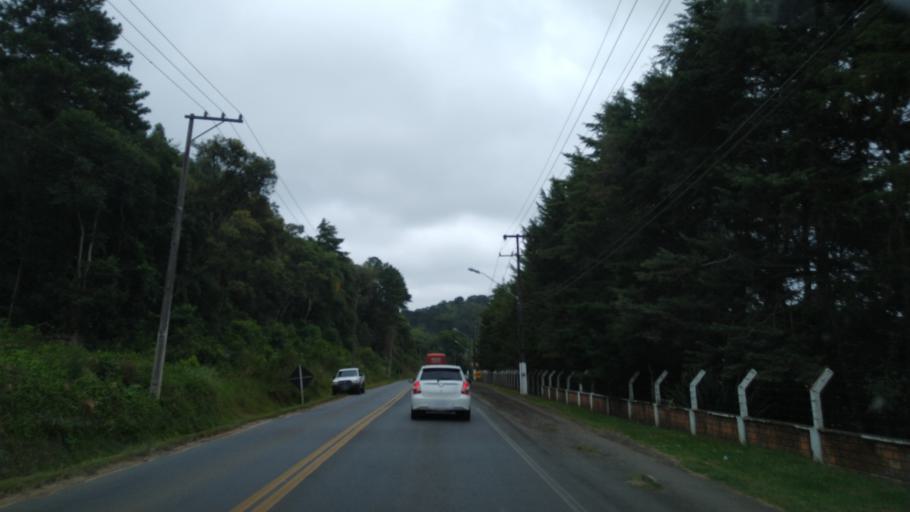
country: BR
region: Parana
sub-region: Uniao Da Vitoria
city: Uniao da Vitoria
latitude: -26.2508
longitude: -51.1128
